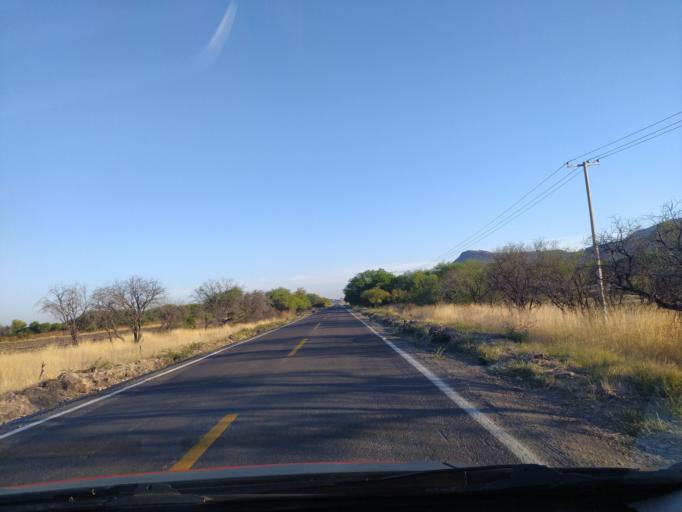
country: MX
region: Guanajuato
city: Ciudad Manuel Doblado
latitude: 20.7741
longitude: -101.8316
